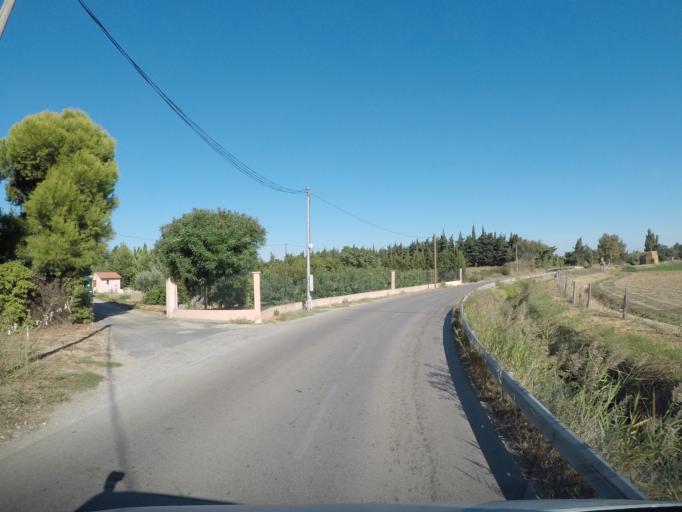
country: FR
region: Languedoc-Roussillon
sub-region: Departement de l'Aude
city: Narbonne
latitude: 43.1629
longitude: 3.0112
